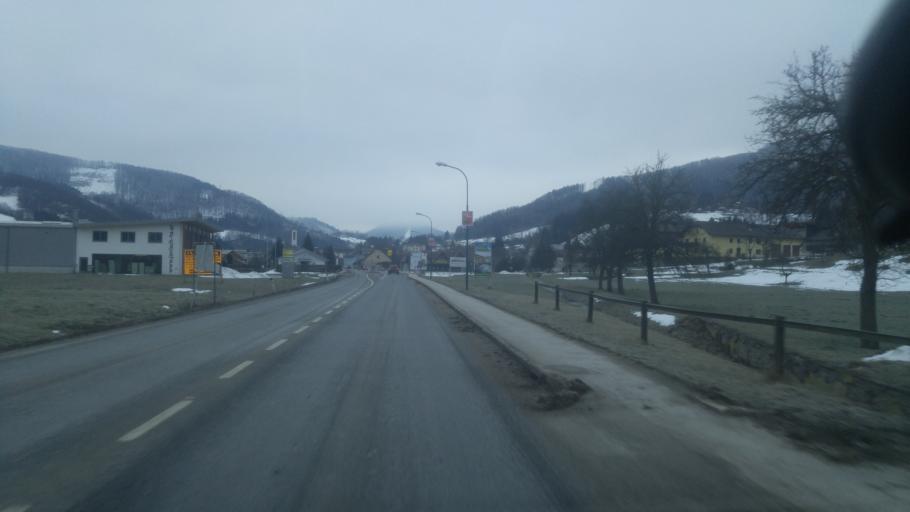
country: AT
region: Lower Austria
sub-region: Politischer Bezirk Lilienfeld
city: Traisen
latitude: 48.0475
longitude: 15.6097
